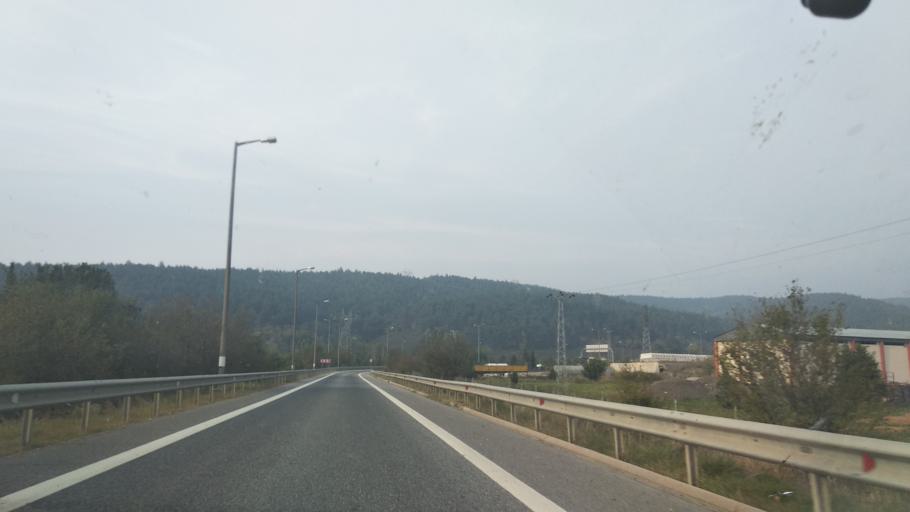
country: TR
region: Duzce
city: Kaynasli
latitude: 40.7856
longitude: 31.2772
